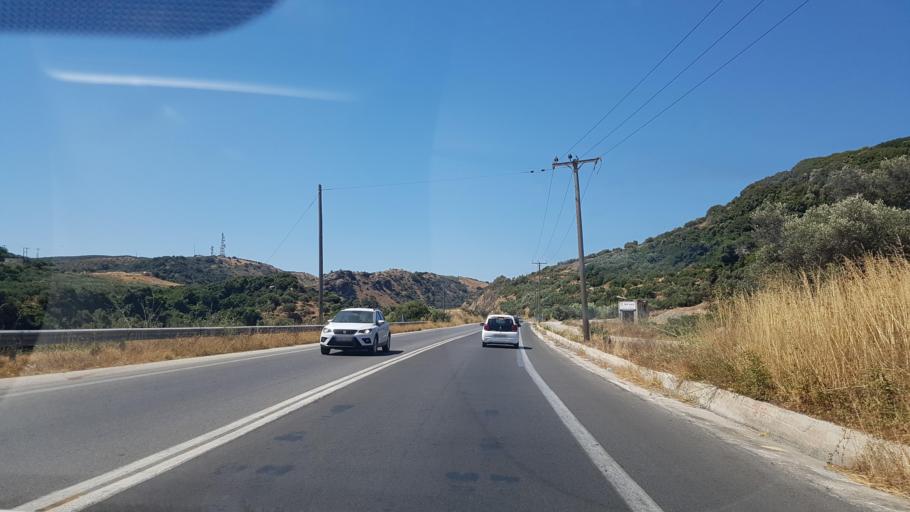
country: GR
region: Crete
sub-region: Nomos Chanias
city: Kolympari
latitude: 35.5219
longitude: 23.7465
